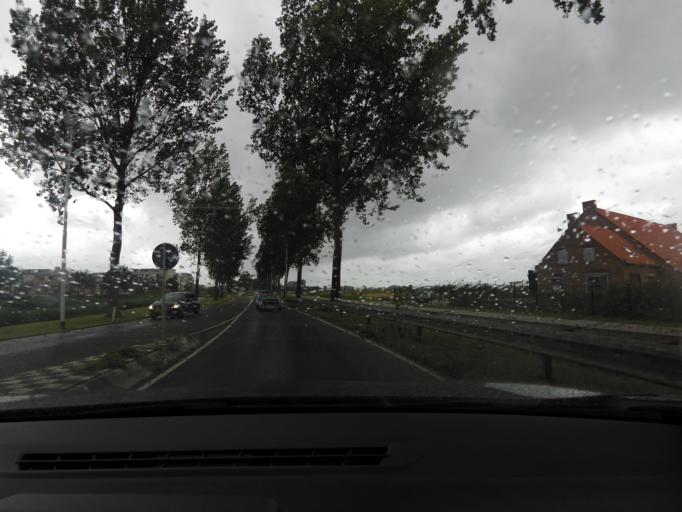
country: NL
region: South Holland
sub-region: Gemeente Hellevoetsluis
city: Nieuwenhoorn
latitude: 51.8443
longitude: 4.1681
